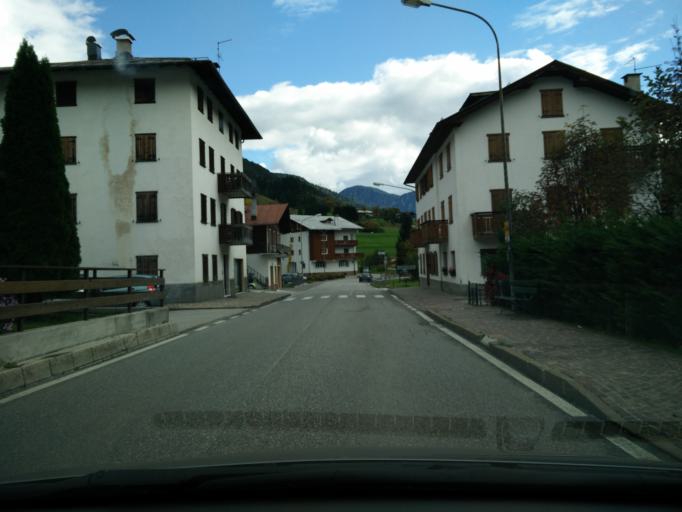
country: IT
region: Veneto
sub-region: Provincia di Belluno
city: Auronzo
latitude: 46.5577
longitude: 12.4262
